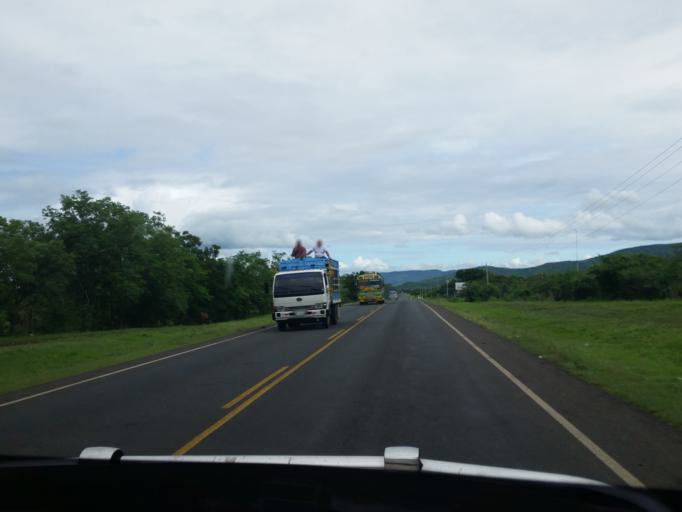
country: NI
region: Managua
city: Tipitapa
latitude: 12.3863
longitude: -86.0448
